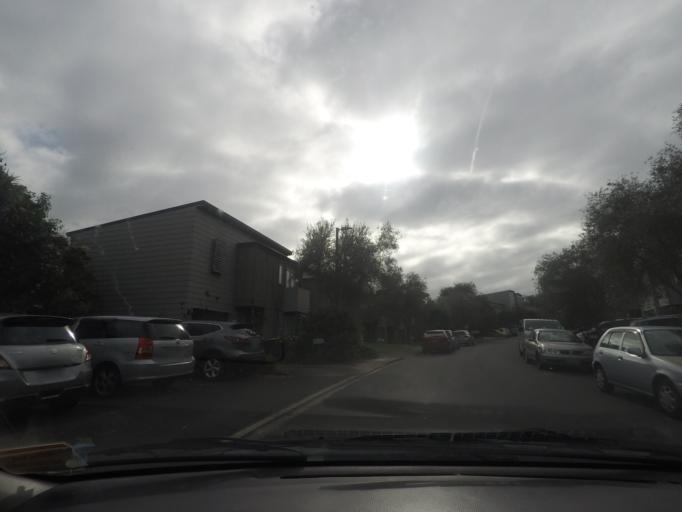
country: NZ
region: Auckland
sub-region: Auckland
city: Waitakere
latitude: -36.9077
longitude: 174.6322
